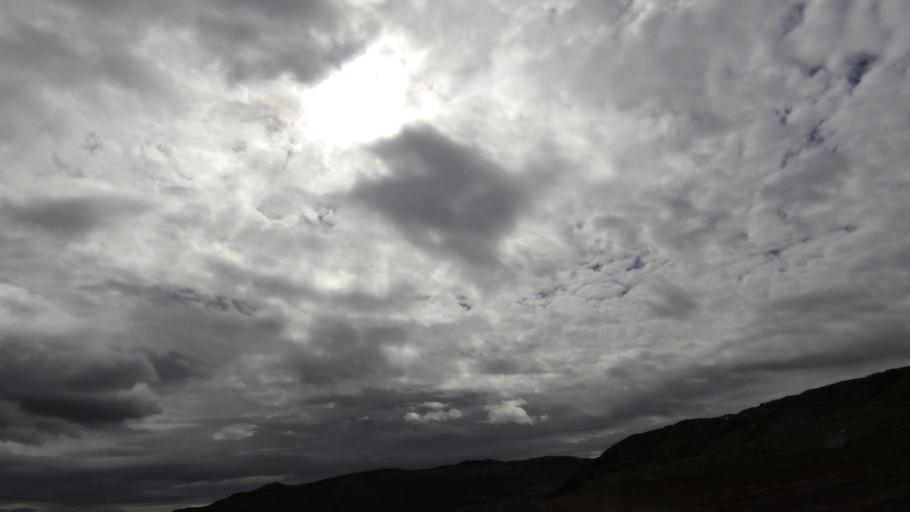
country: IS
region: West
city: Stykkisholmur
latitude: 65.5364
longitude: -22.0771
